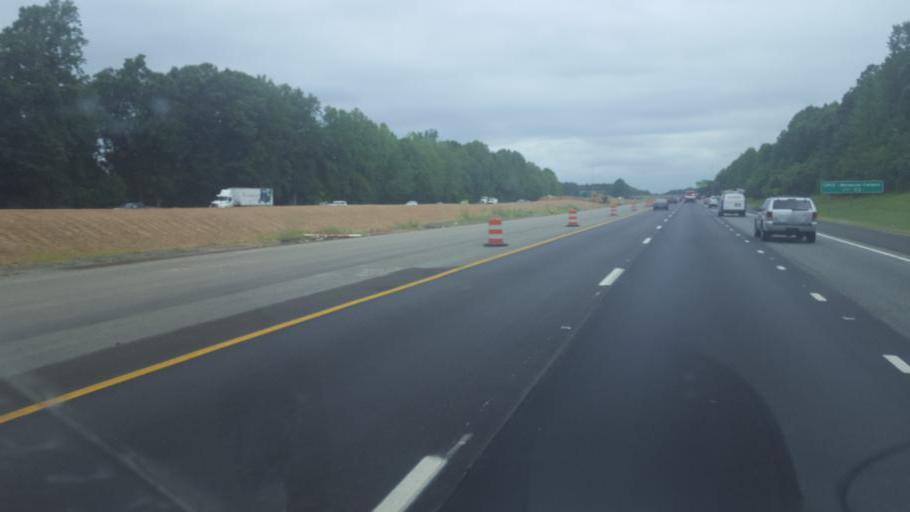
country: US
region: North Carolina
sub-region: Mecklenburg County
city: Huntersville
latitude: 35.4015
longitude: -80.8560
